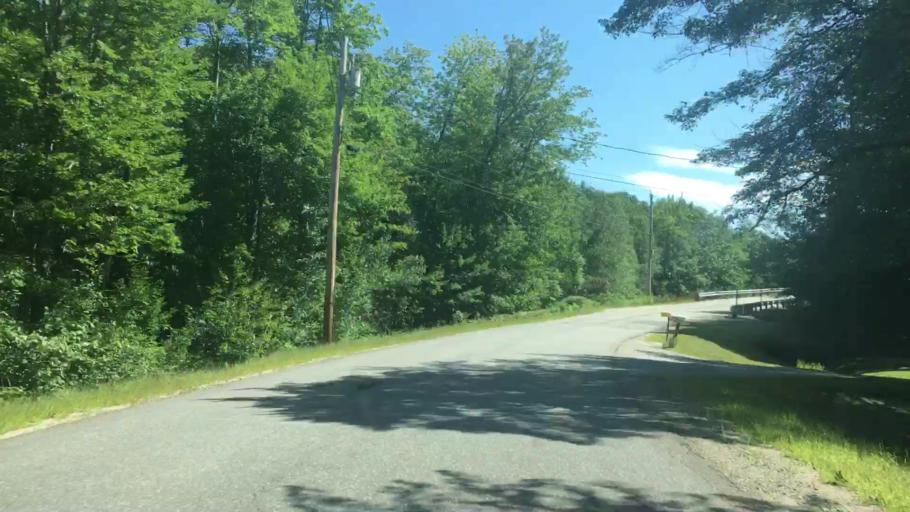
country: US
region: Maine
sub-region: Androscoggin County
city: Sabattus
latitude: 44.1256
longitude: -70.0370
